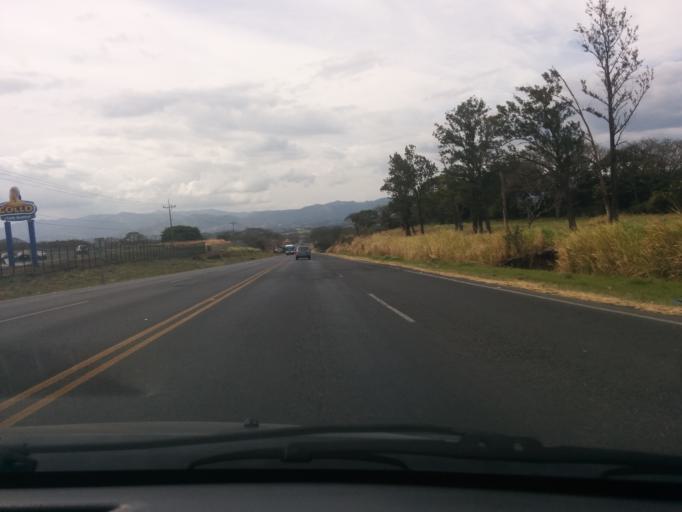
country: CR
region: Alajuela
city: Carrillos
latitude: 9.9986
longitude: -84.2769
